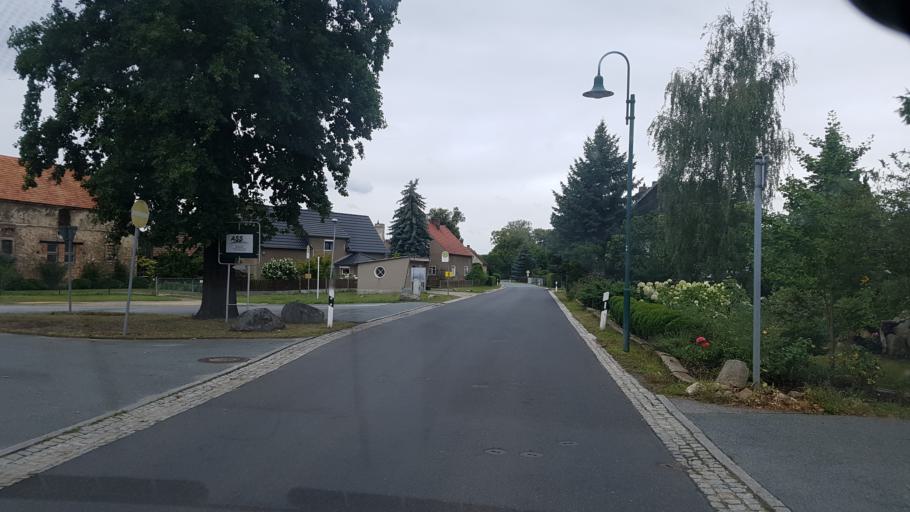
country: DE
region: Saxony
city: Kodersdorf
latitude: 51.2265
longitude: 14.8593
